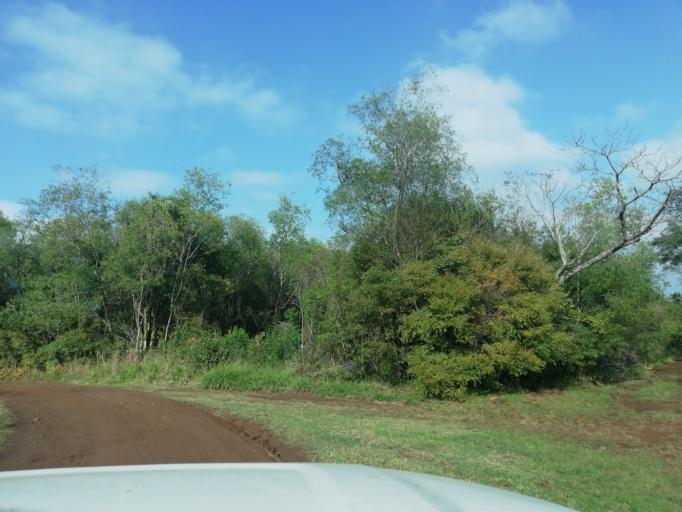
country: AR
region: Misiones
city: Cerro Azul
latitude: -27.5828
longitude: -55.5185
